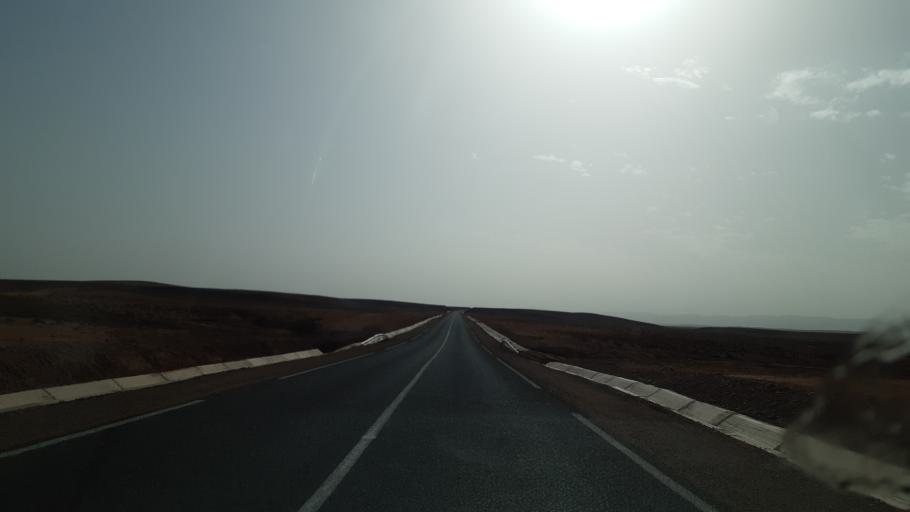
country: MA
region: Meknes-Tafilalet
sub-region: Khenifra
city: Midelt
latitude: 32.8890
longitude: -4.7434
